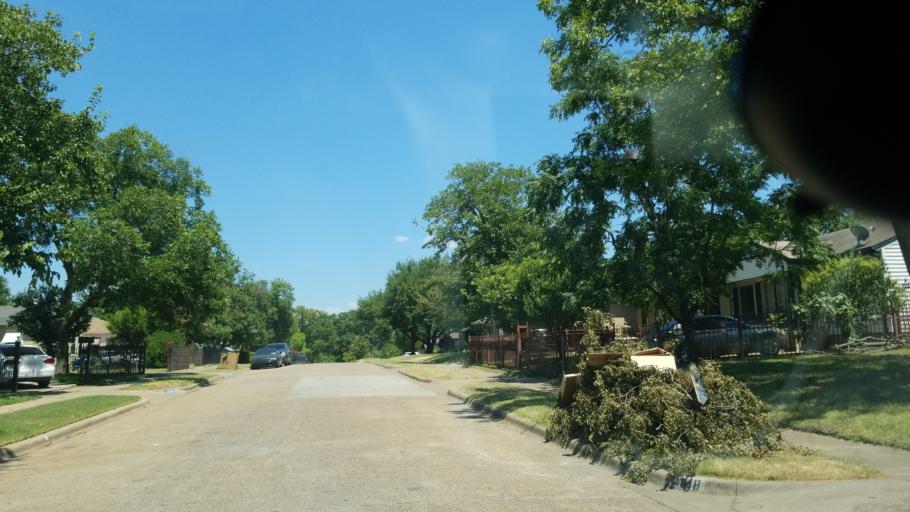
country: US
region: Texas
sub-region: Dallas County
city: Cockrell Hill
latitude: 32.7262
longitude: -96.8506
